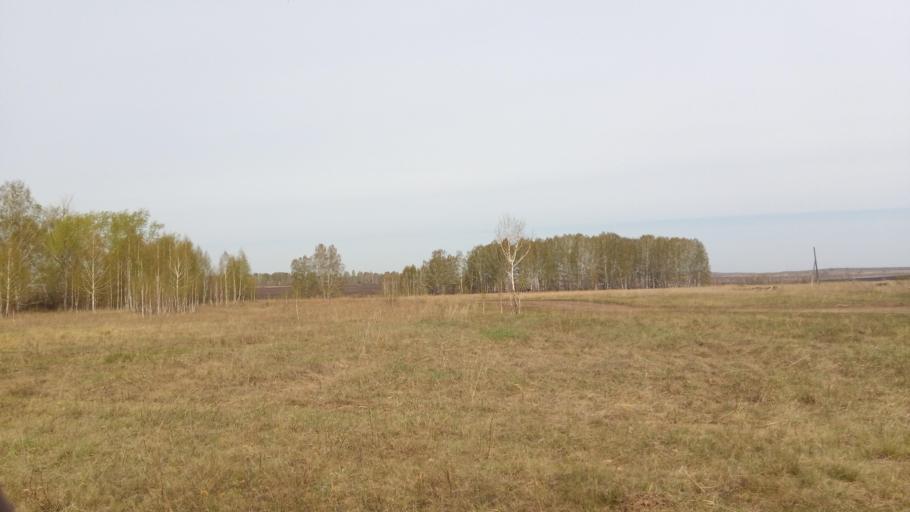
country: RU
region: Chelyabinsk
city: Timiryazevskiy
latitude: 55.0256
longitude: 60.8600
